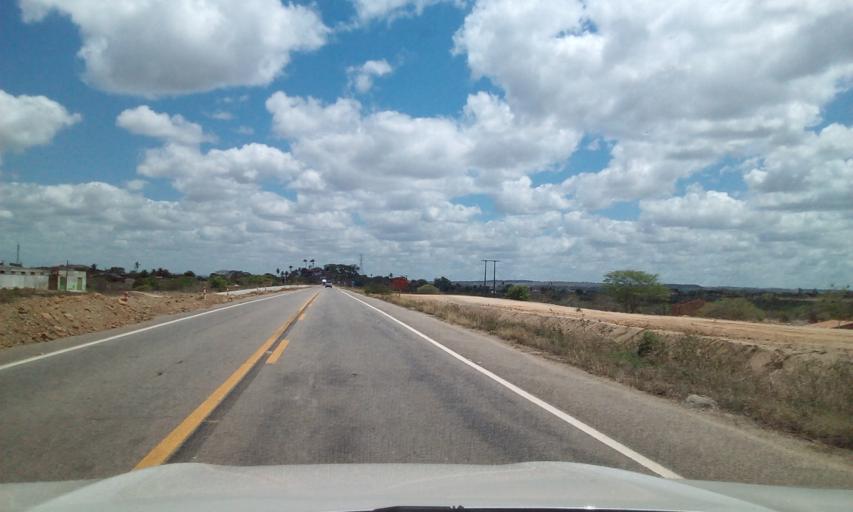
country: BR
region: Sergipe
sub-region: Propria
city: Propria
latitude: -10.2219
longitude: -36.8297
